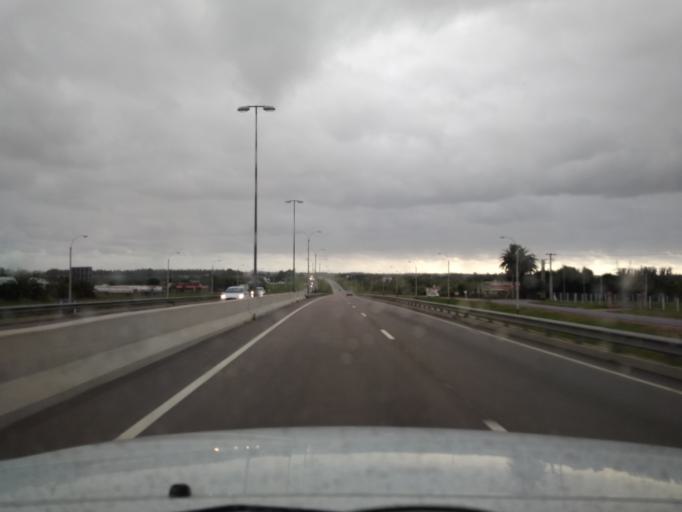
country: UY
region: Canelones
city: Las Piedras
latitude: -34.7228
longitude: -56.2465
